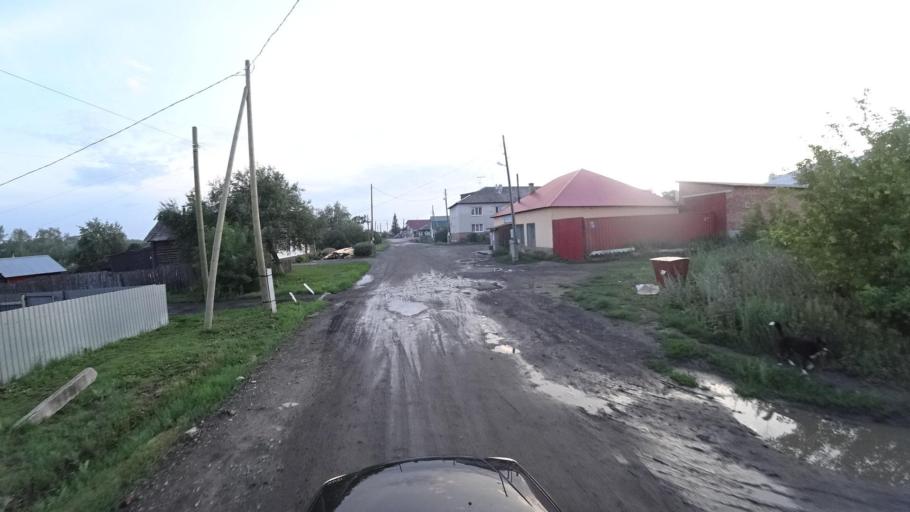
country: RU
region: Sverdlovsk
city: Kamyshlov
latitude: 56.8574
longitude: 62.7104
